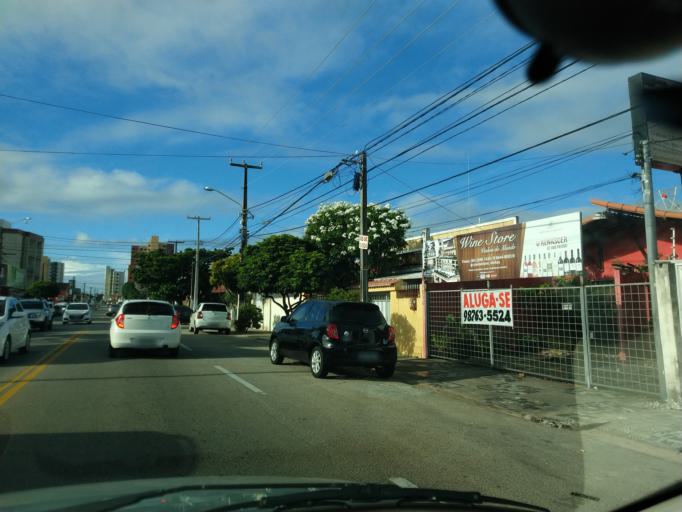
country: BR
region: Rio Grande do Norte
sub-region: Natal
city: Natal
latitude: -5.7998
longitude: -35.2115
